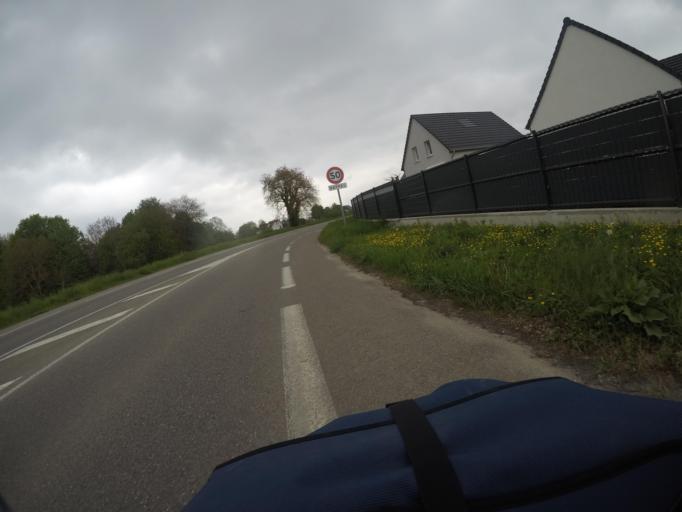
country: DE
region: Baden-Wuerttemberg
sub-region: Karlsruhe Region
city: Greffern
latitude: 48.7941
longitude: 7.9944
